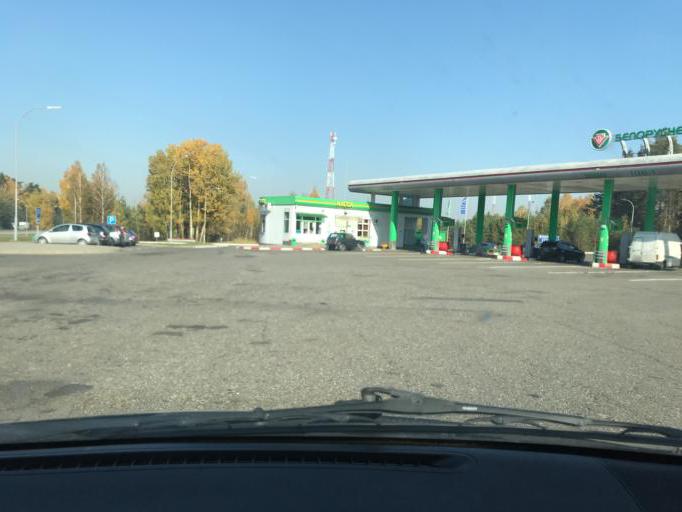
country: BY
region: Minsk
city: Uzda
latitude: 53.4263
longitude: 27.4950
